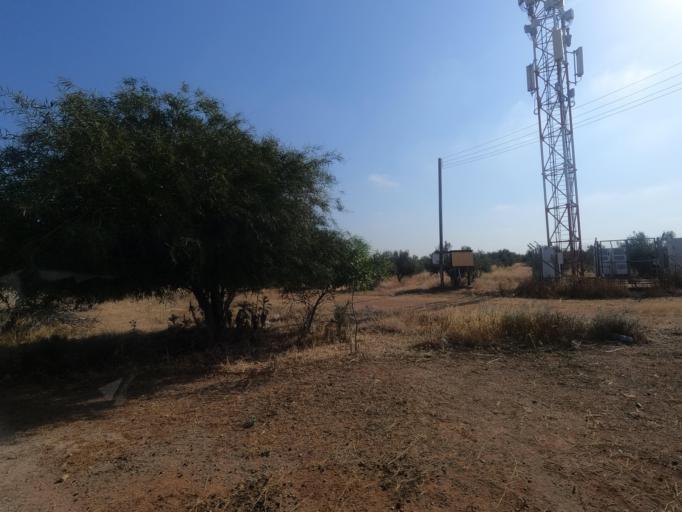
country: CY
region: Ammochostos
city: Avgorou
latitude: 35.0453
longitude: 33.8300
